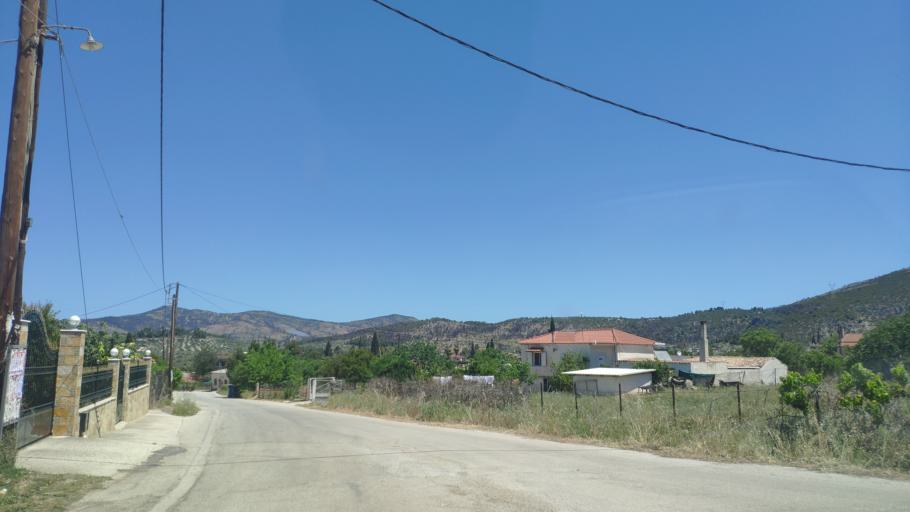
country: GR
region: Peloponnese
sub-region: Nomos Korinthias
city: Athikia
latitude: 37.8167
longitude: 22.9241
